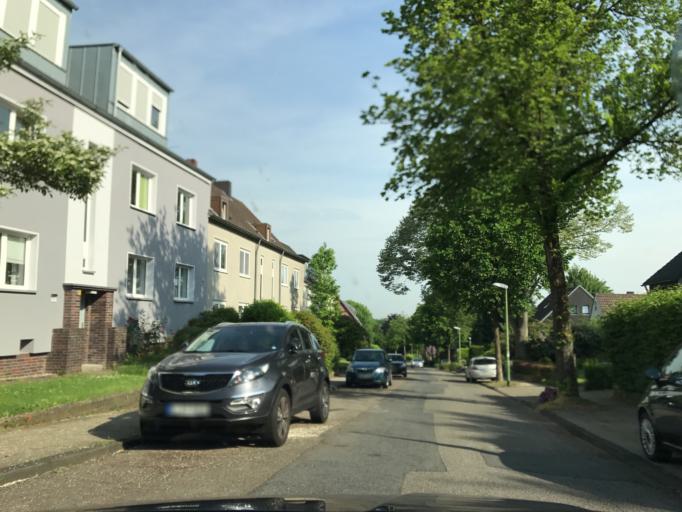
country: DE
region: North Rhine-Westphalia
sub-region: Regierungsbezirk Dusseldorf
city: Essen
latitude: 51.4146
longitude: 6.9907
